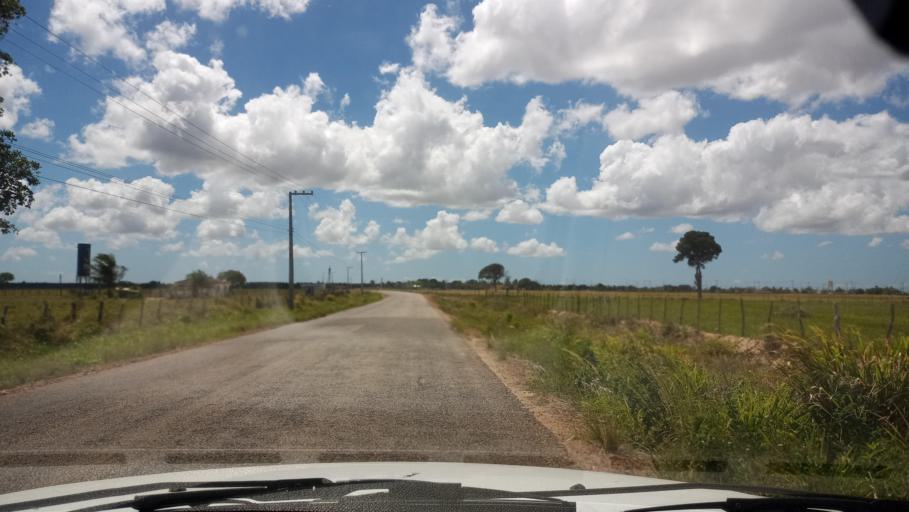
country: BR
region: Rio Grande do Norte
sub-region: Brejinho
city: Brejinho
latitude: -6.0388
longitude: -35.3956
